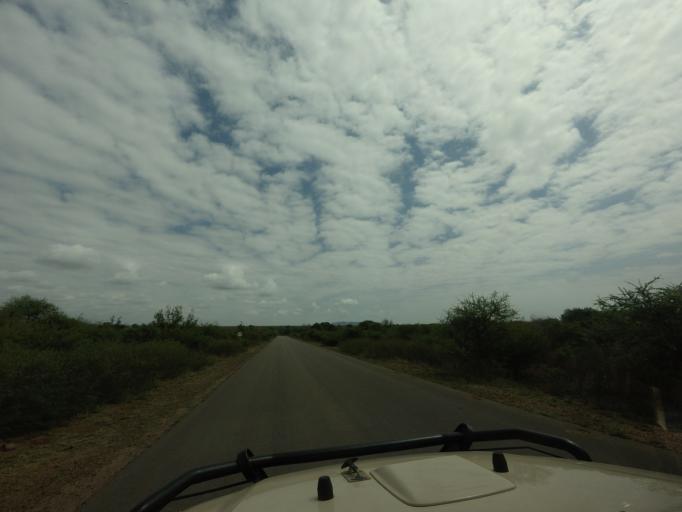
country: ZA
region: Mpumalanga
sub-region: Ehlanzeni District
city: Komatipoort
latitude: -25.1199
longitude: 31.9139
